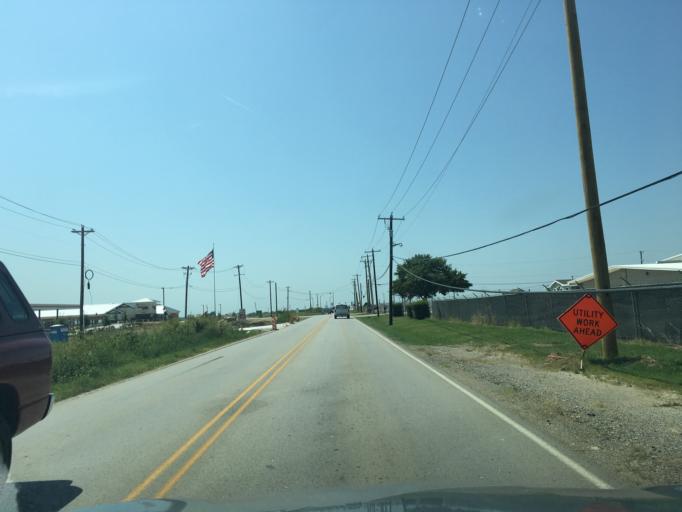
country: US
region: Texas
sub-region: Tarrant County
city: Blue Mound
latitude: 32.9032
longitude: -97.3317
